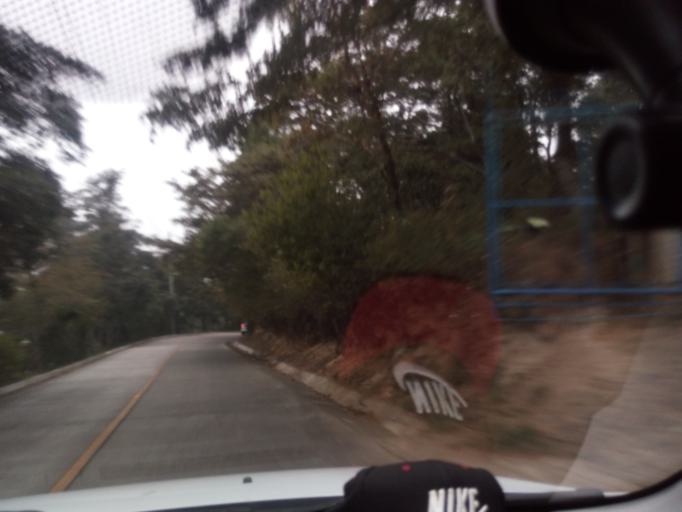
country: GT
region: Sacatepequez
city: Santa Lucia Milpas Altas
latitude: 14.5882
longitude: -90.7090
